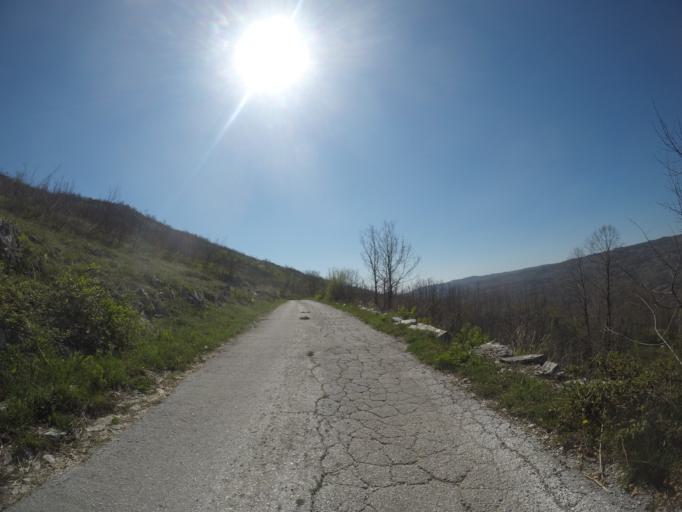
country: ME
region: Danilovgrad
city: Danilovgrad
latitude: 42.5371
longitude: 19.0139
